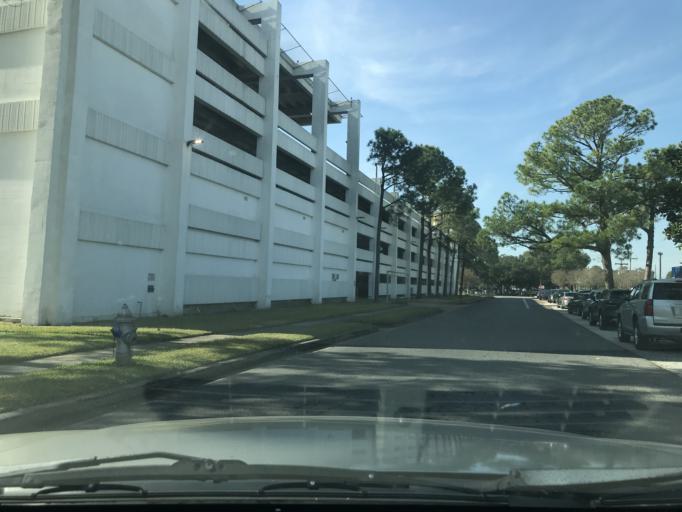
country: US
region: Louisiana
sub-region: Jefferson Parish
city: Marrero
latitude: 29.8932
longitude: -90.0946
